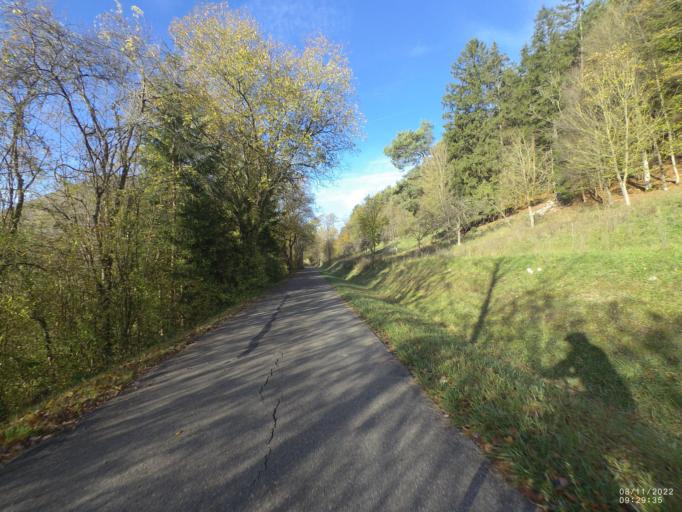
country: DE
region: Baden-Wuerttemberg
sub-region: Regierungsbezirk Stuttgart
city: Bad Uberkingen
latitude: 48.6013
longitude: 9.7862
